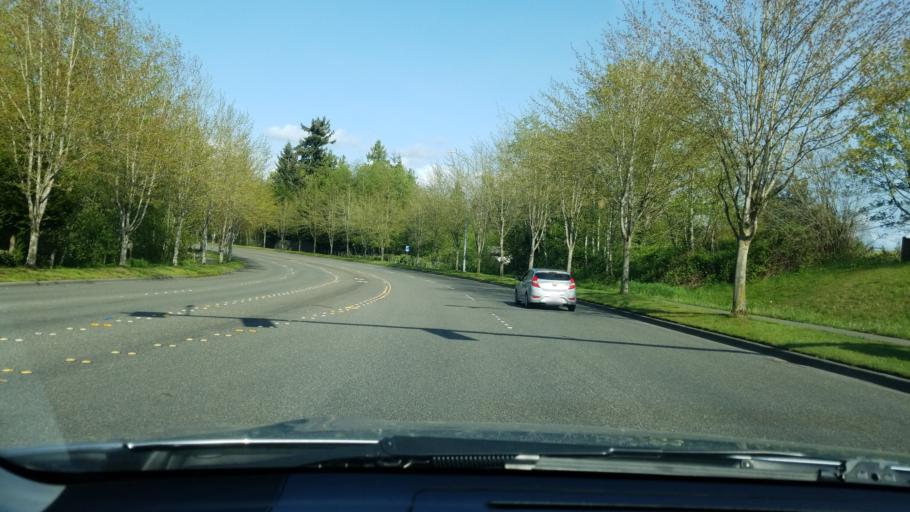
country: US
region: Washington
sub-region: Snohomish County
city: Alderwood Manor
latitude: 47.8186
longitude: -122.2744
